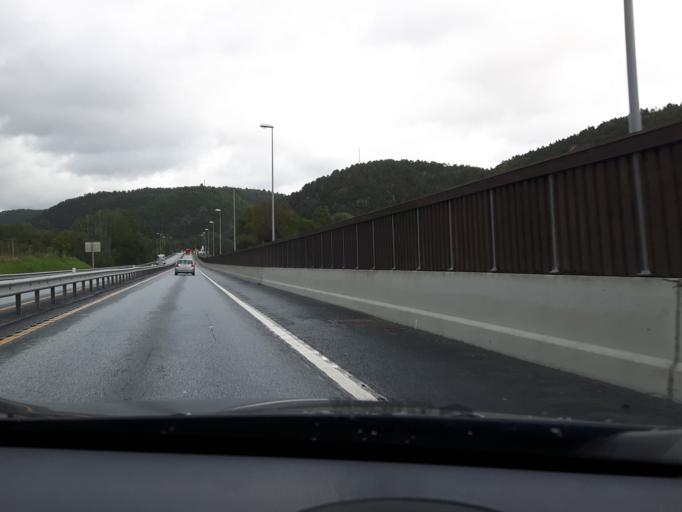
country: NO
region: Vest-Agder
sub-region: Songdalen
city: Nodeland
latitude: 58.1291
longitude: 7.8552
